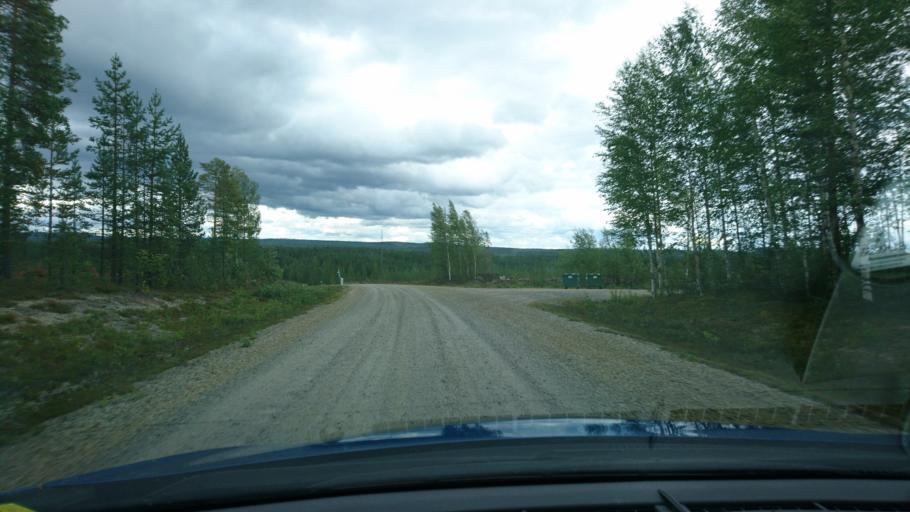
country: SE
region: Vaesterbotten
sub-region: Norsjo Kommun
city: Norsjoe
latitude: 64.5069
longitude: 19.2882
